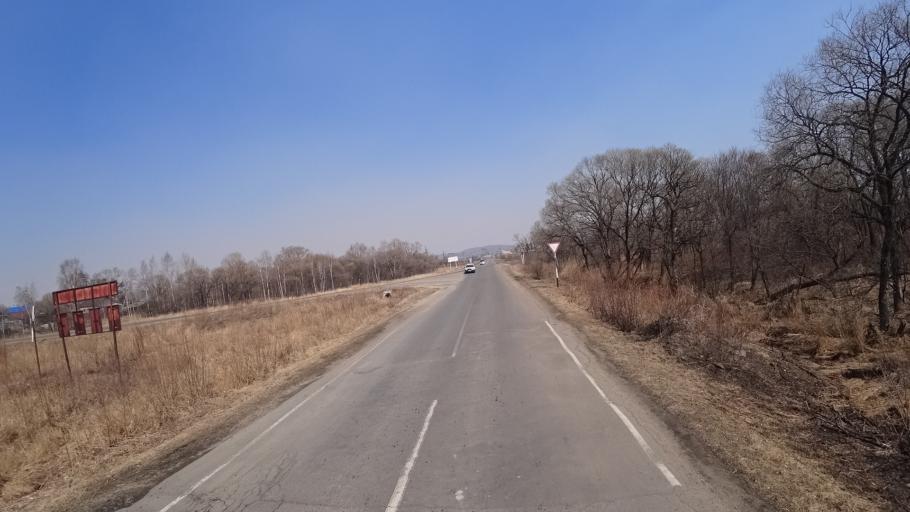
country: RU
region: Amur
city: Novobureyskiy
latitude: 49.7895
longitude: 129.8492
